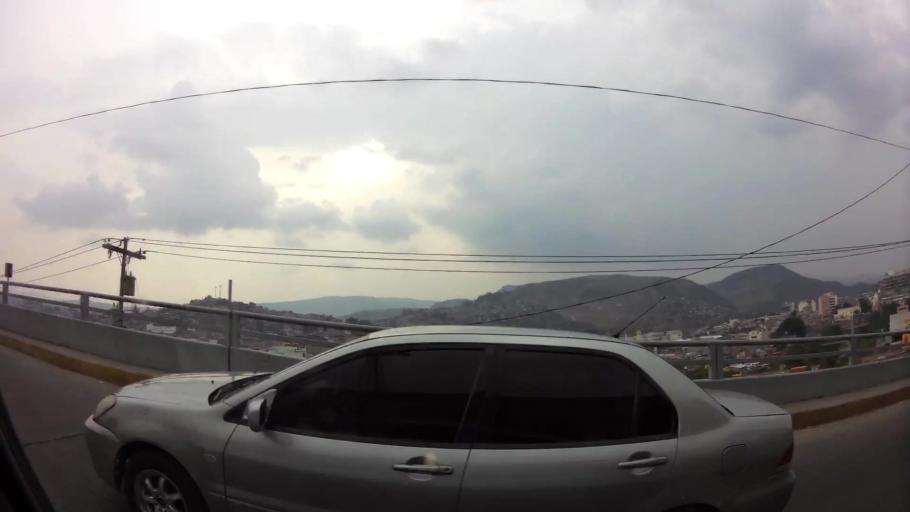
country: HN
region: Francisco Morazan
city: Tegucigalpa
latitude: 14.0988
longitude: -87.2049
